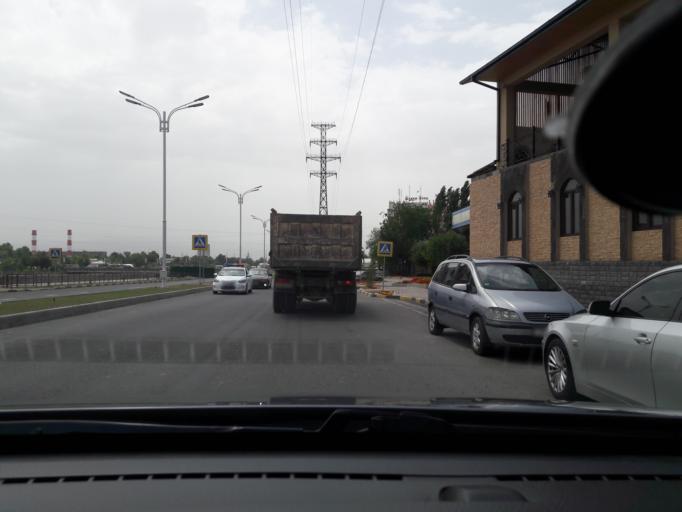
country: TJ
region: Dushanbe
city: Dushanbe
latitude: 38.5630
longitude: 68.7692
